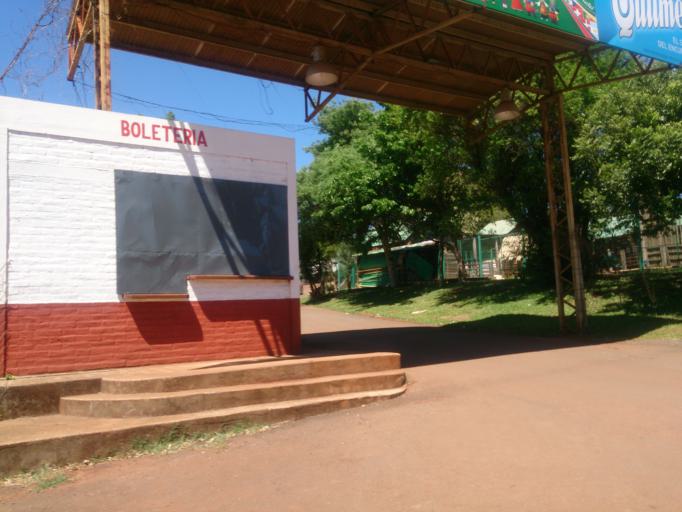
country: AR
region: Misiones
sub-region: Departamento de Obera
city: Obera
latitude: -27.4976
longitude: -55.1133
